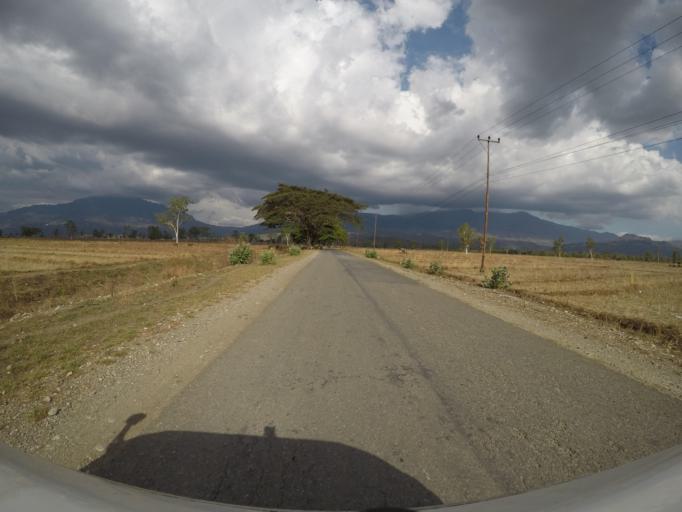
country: TL
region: Bobonaro
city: Maliana
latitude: -8.9882
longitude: 125.1670
